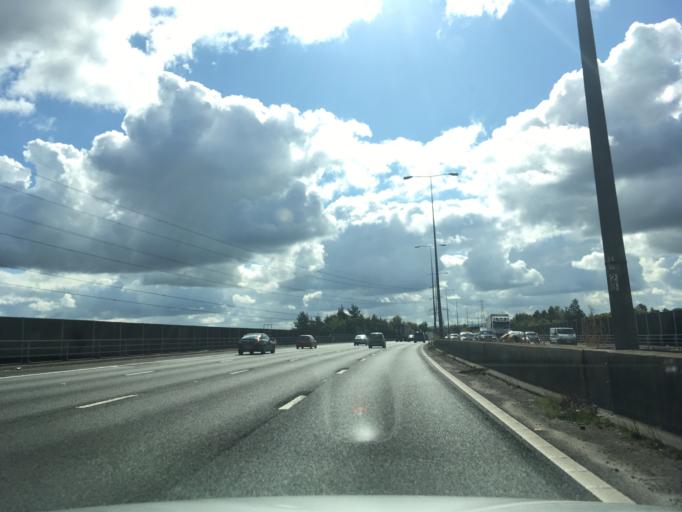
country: GB
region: England
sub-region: Surrey
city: Byfleet
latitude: 51.3490
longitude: -0.4865
